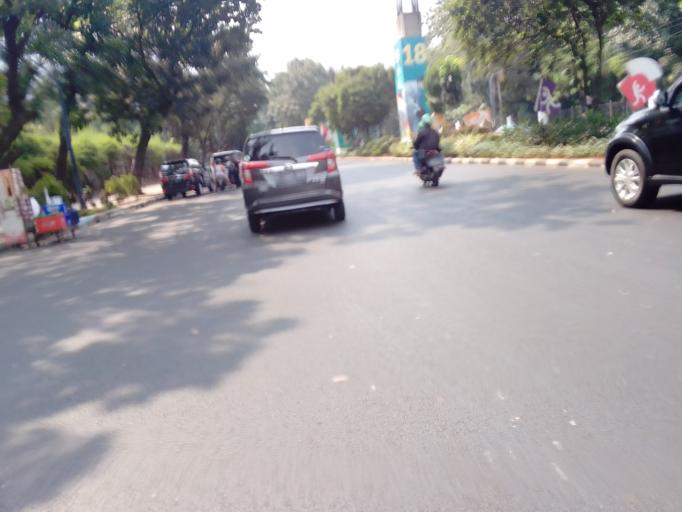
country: ID
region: Jakarta Raya
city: Jakarta
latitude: -6.2173
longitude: 106.7982
